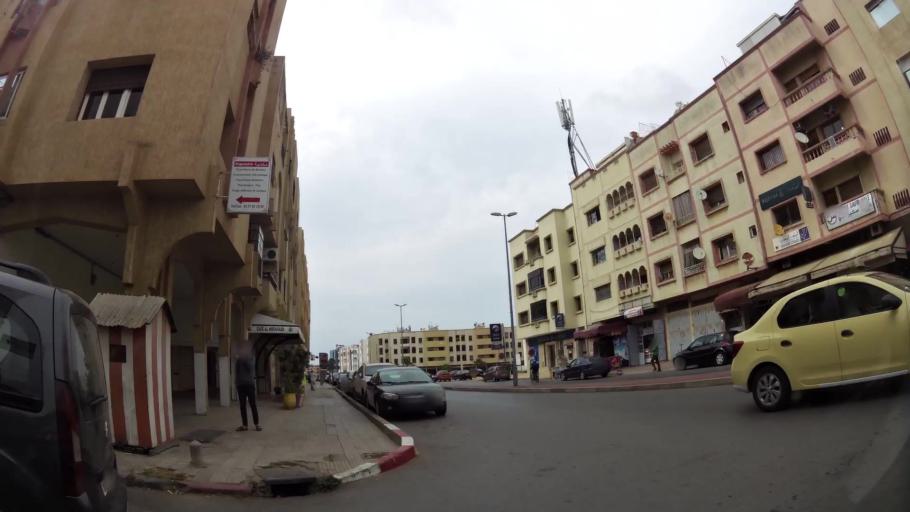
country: MA
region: Rabat-Sale-Zemmour-Zaer
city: Sale
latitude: 34.0295
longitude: -6.8011
